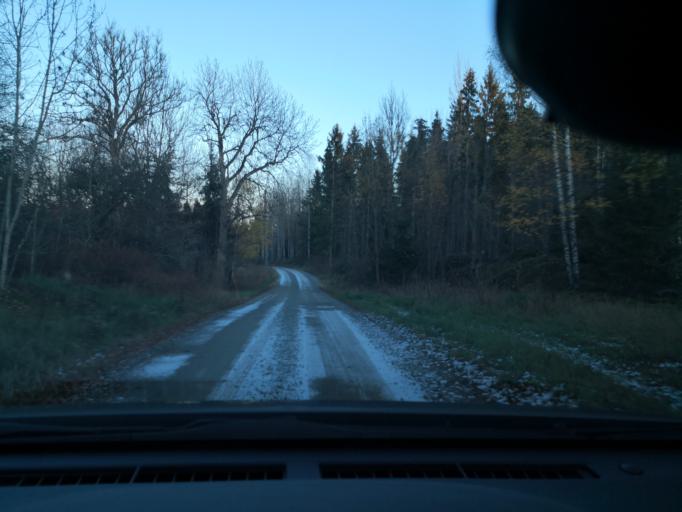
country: SE
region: Vaestmanland
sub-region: Vasteras
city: Tillberga
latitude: 59.7640
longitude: 16.6205
